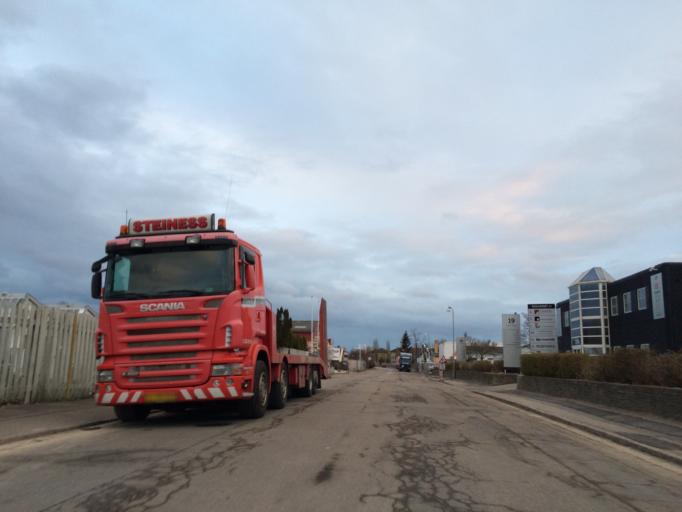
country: DK
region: Capital Region
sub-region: Hoje-Taastrup Kommune
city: Taastrup
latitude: 55.6496
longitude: 12.2907
